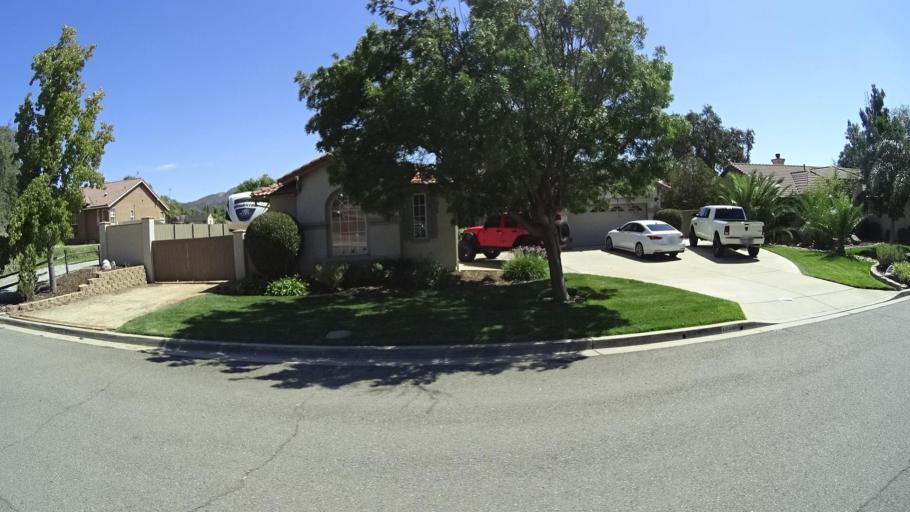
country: US
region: California
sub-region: San Diego County
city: San Diego Country Estates
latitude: 33.0186
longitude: -116.8195
